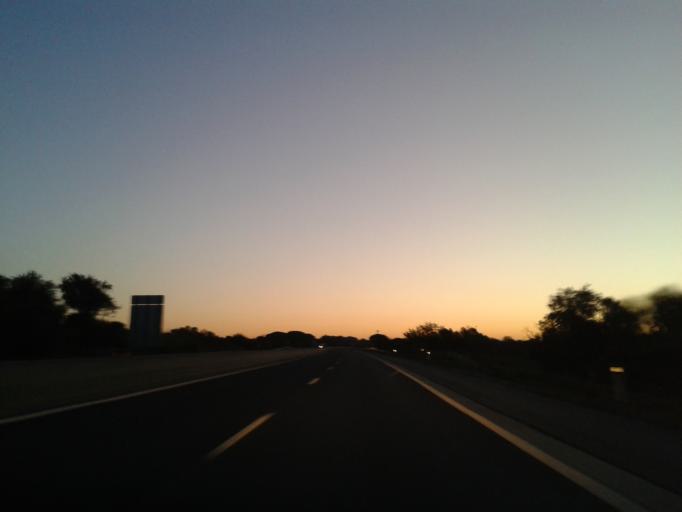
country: PT
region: Faro
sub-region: Silves
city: Armacao de Pera
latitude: 37.1379
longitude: -8.3405
